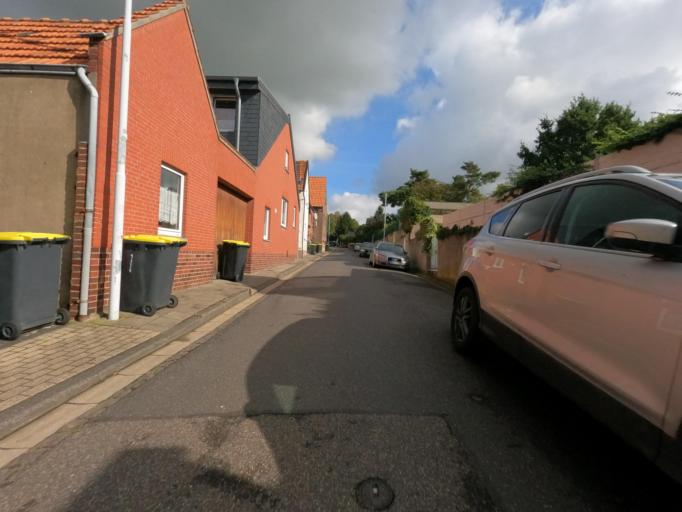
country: DE
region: North Rhine-Westphalia
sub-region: Regierungsbezirk Koln
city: Linnich
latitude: 51.0041
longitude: 6.2818
